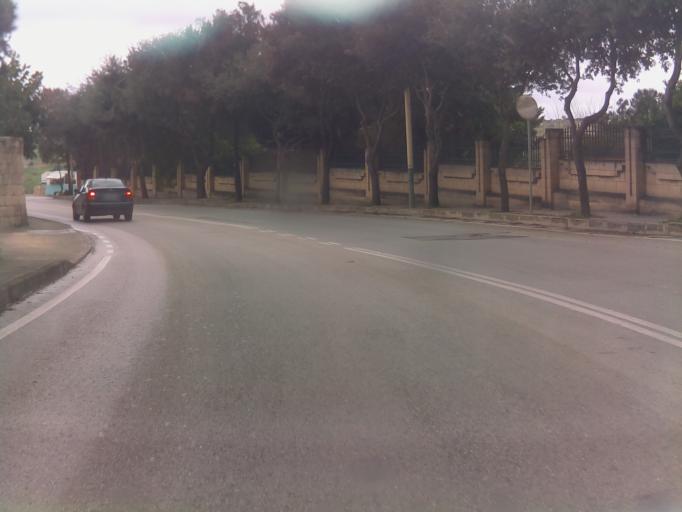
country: MT
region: Il-Mosta
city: Mosta
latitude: 35.9173
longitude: 14.4163
